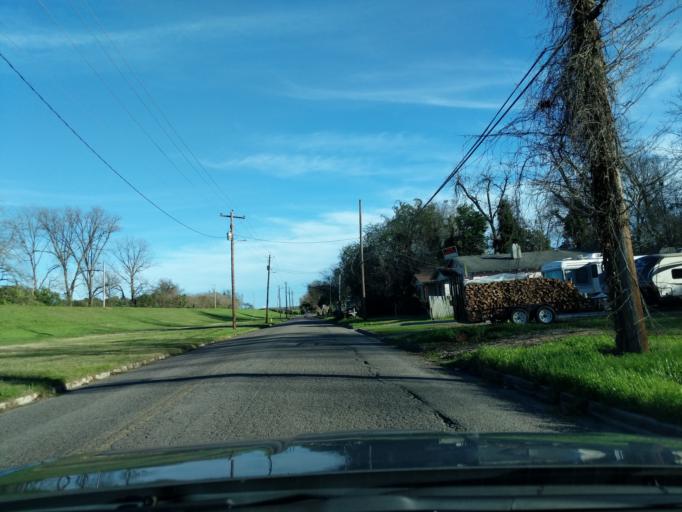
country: US
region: Georgia
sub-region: Richmond County
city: Augusta
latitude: 33.4713
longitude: -81.9507
